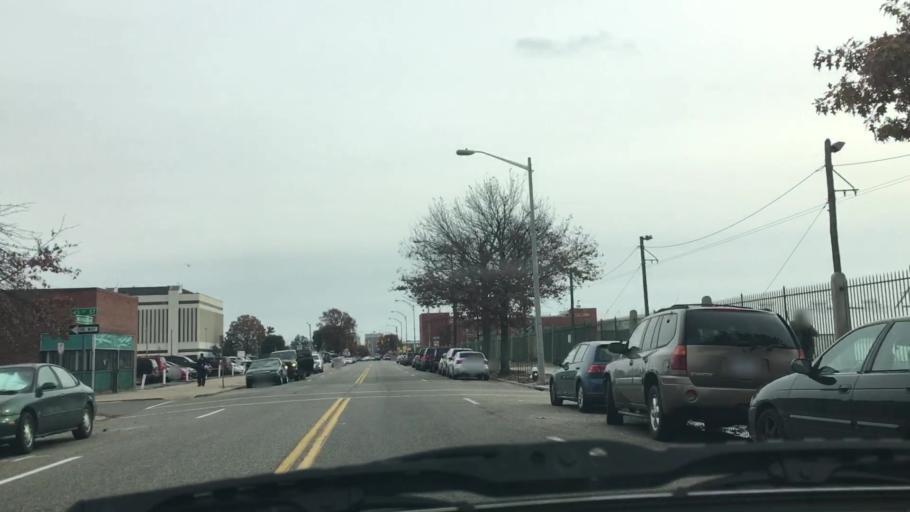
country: US
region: Virginia
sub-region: City of Newport News
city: Newport News
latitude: 36.9909
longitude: -76.4385
